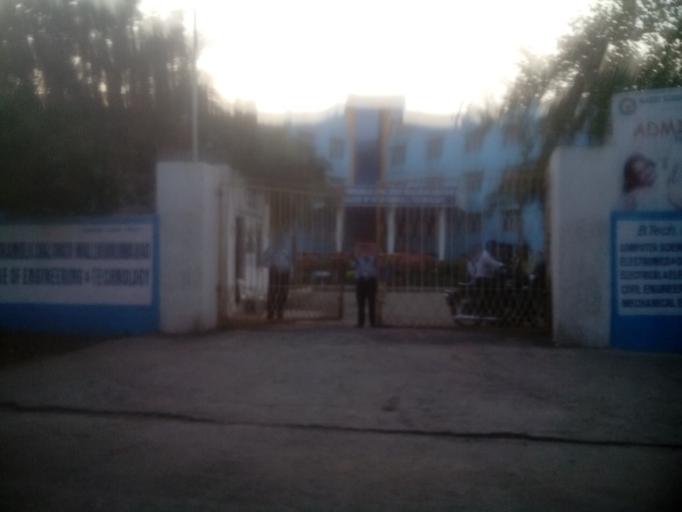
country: IN
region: Andhra Pradesh
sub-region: Krishna
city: Vijayawada
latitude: 16.5238
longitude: 80.6143
